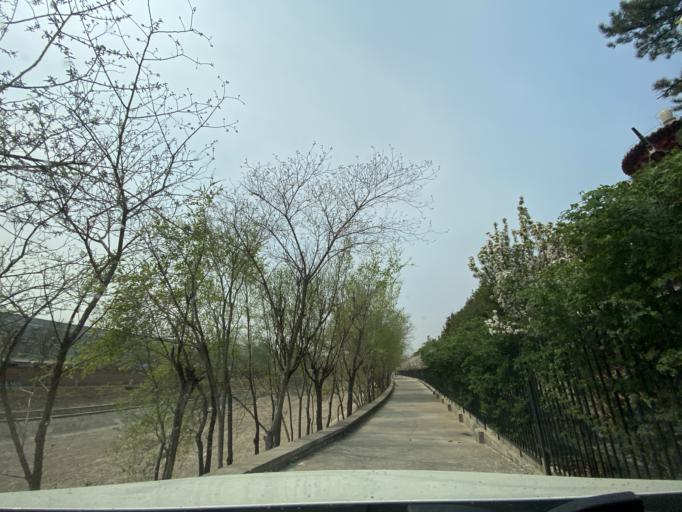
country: CN
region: Beijing
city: Sijiqing
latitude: 39.9398
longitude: 116.2503
